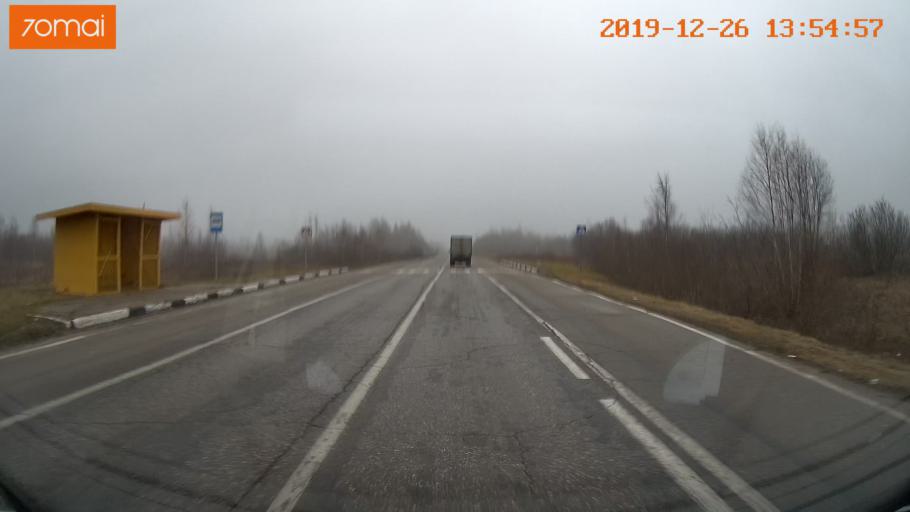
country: RU
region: Jaroslavl
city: Poshekhon'ye
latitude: 58.6084
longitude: 38.6416
